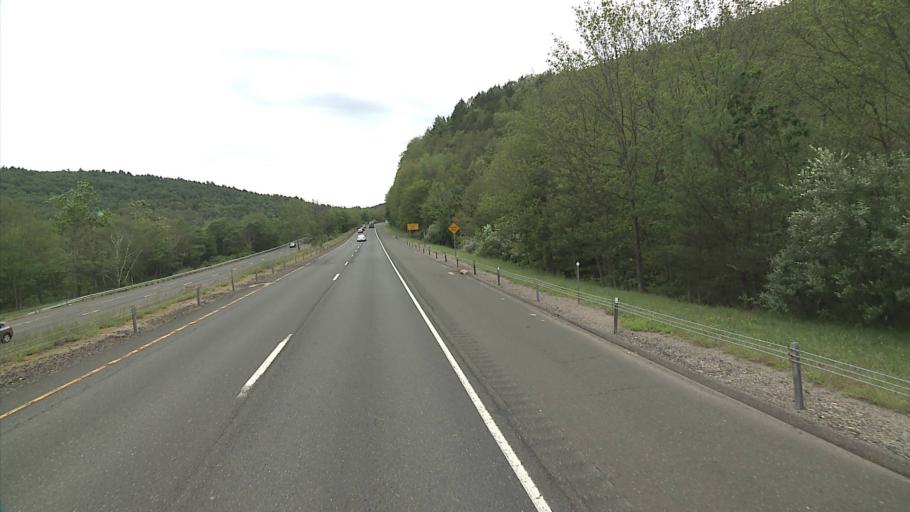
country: US
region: Connecticut
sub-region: Litchfield County
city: Thomaston
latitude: 41.6392
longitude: -73.0807
